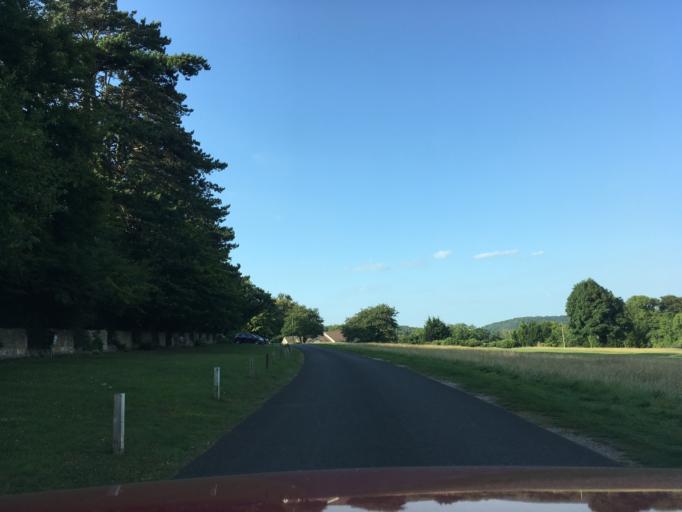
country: GB
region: England
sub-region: Gloucestershire
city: Painswick
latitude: 51.7963
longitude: -2.1910
